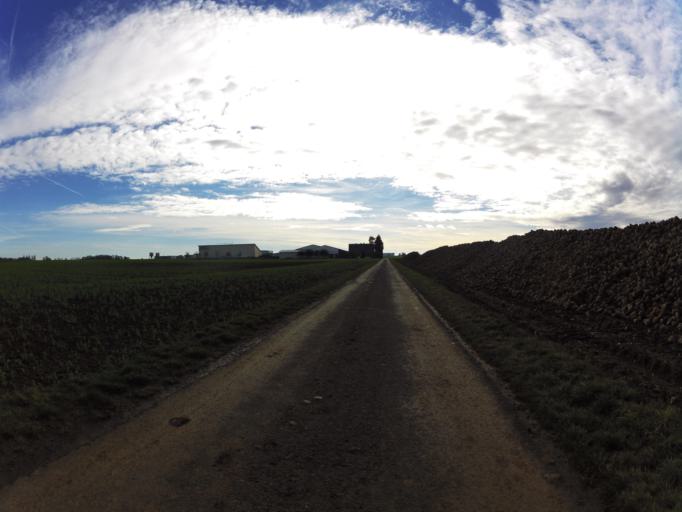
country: DE
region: Bavaria
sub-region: Regierungsbezirk Unterfranken
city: Giebelstadt
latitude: 49.6600
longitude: 9.9531
